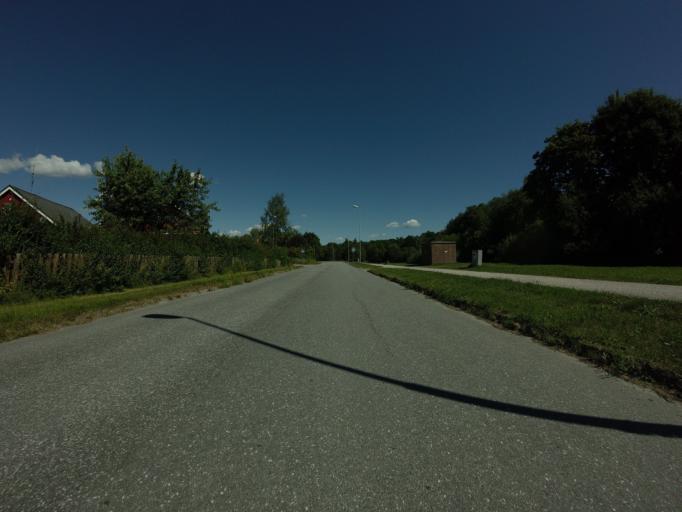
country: SE
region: Stockholm
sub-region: Sollentuna Kommun
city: Sollentuna
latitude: 59.4557
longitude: 17.9019
